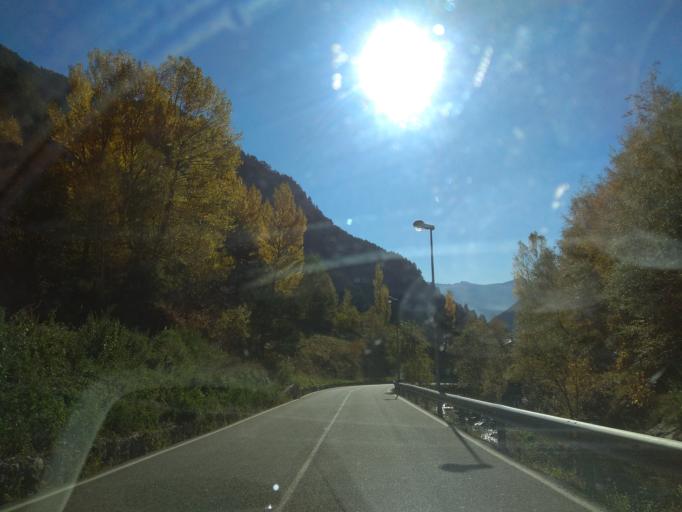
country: AD
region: La Massana
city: Arinsal
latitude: 42.5776
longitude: 1.4801
